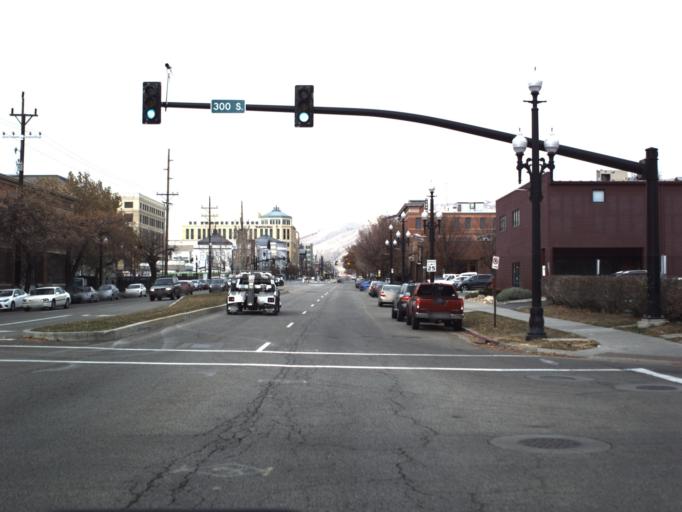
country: US
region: Utah
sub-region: Salt Lake County
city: Salt Lake City
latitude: 40.7628
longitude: -111.9024
